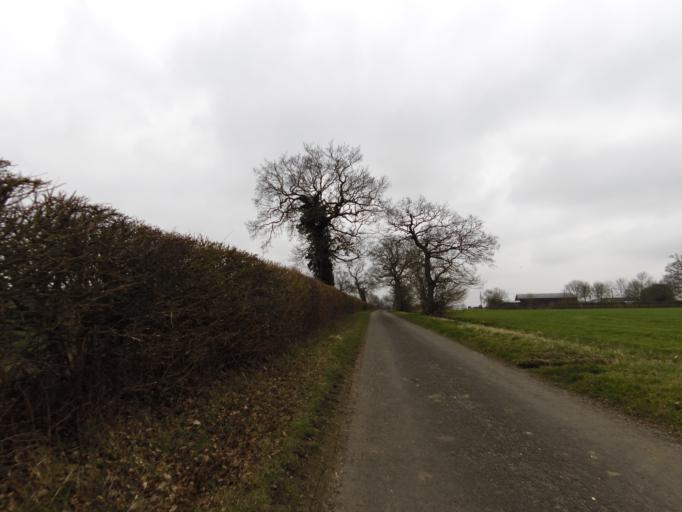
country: GB
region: England
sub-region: Suffolk
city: Framlingham
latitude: 52.2342
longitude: 1.3878
